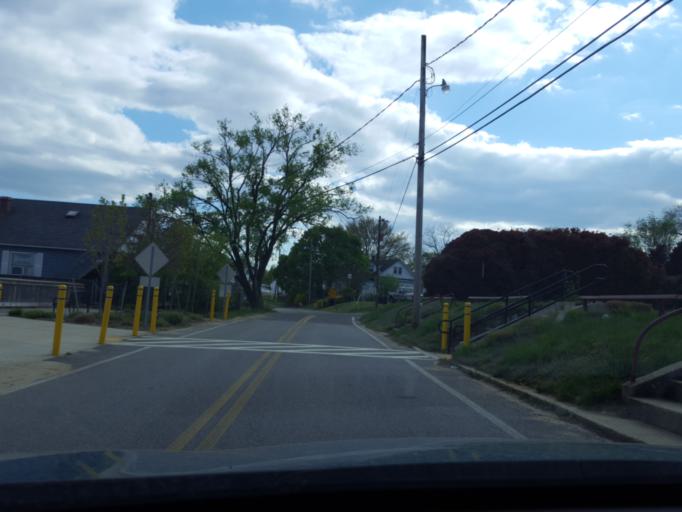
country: US
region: Maryland
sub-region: Saint Mary's County
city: Golden Beach
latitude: 38.5102
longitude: -76.6783
